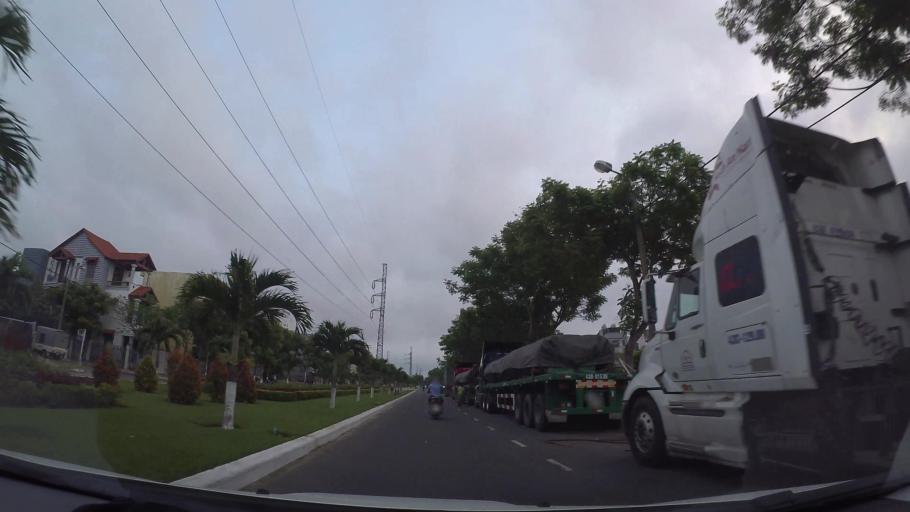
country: VN
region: Da Nang
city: Son Tra
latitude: 16.0419
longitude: 108.2382
